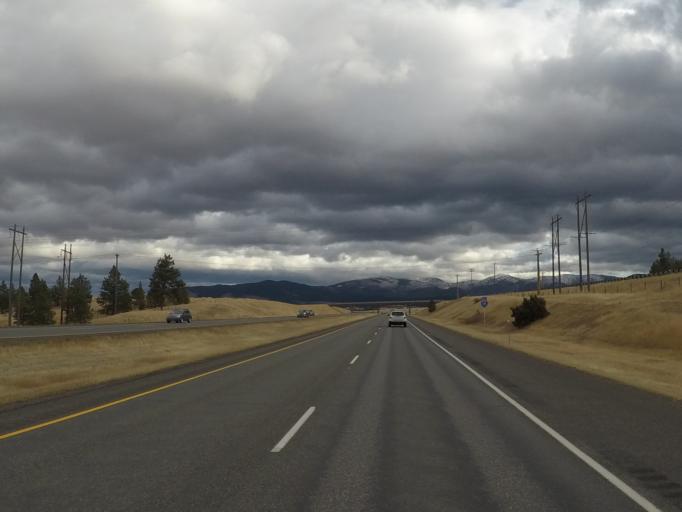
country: US
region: Montana
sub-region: Jefferson County
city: Montana City
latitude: 46.5662
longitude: -111.9623
